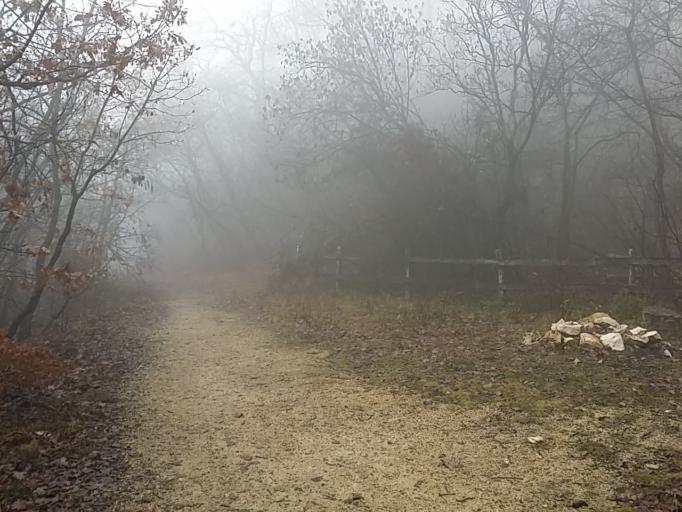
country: HU
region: Pest
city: Budakeszi
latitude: 47.5147
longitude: 18.9693
